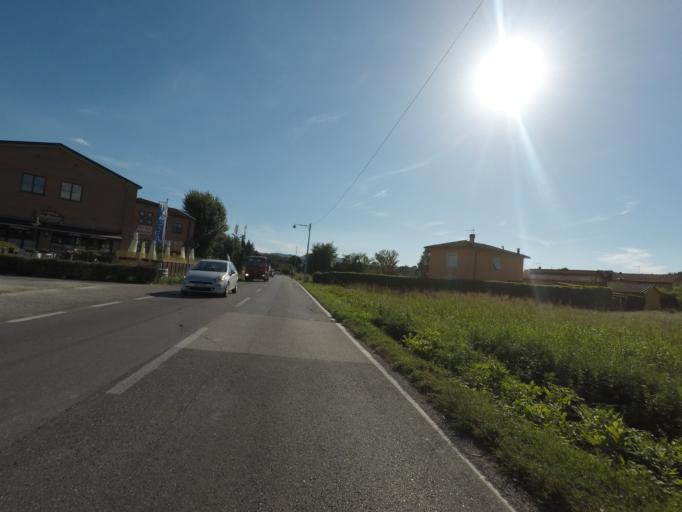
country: IT
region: Tuscany
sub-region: Provincia di Lucca
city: Lucca
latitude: 43.8682
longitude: 10.5122
